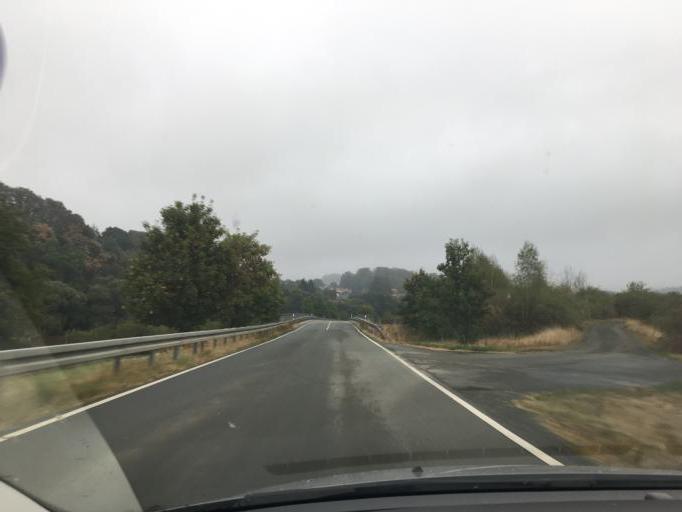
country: DE
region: Thuringia
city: Gorkwitz
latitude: 50.5664
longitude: 11.7782
